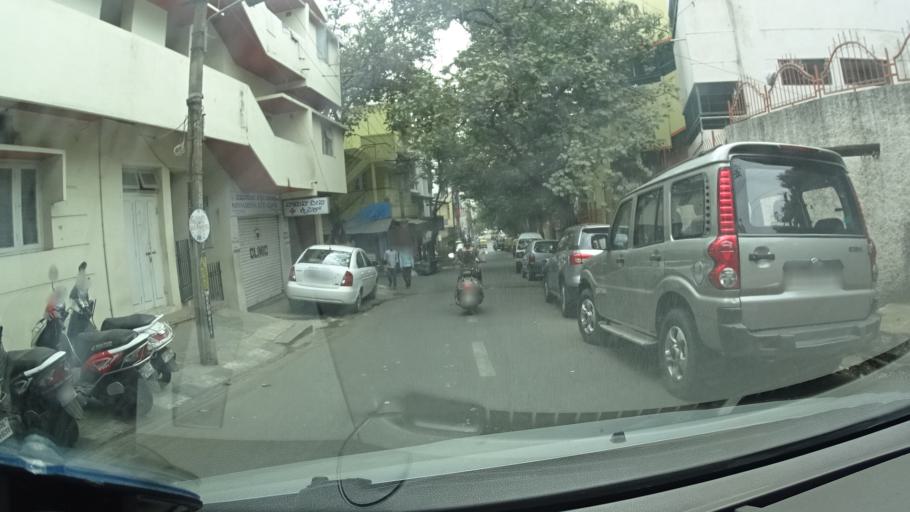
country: IN
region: Karnataka
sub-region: Bangalore Urban
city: Bangalore
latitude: 13.0051
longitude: 77.5505
